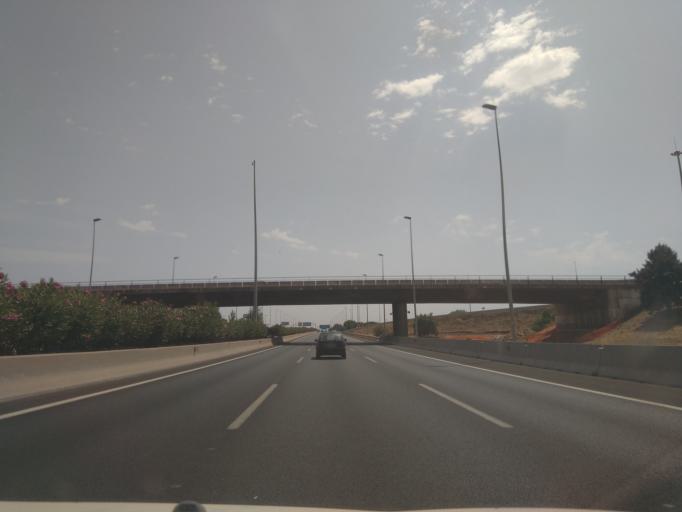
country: ES
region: Valencia
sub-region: Provincia de Valencia
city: Silla
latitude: 39.3650
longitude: -0.4263
